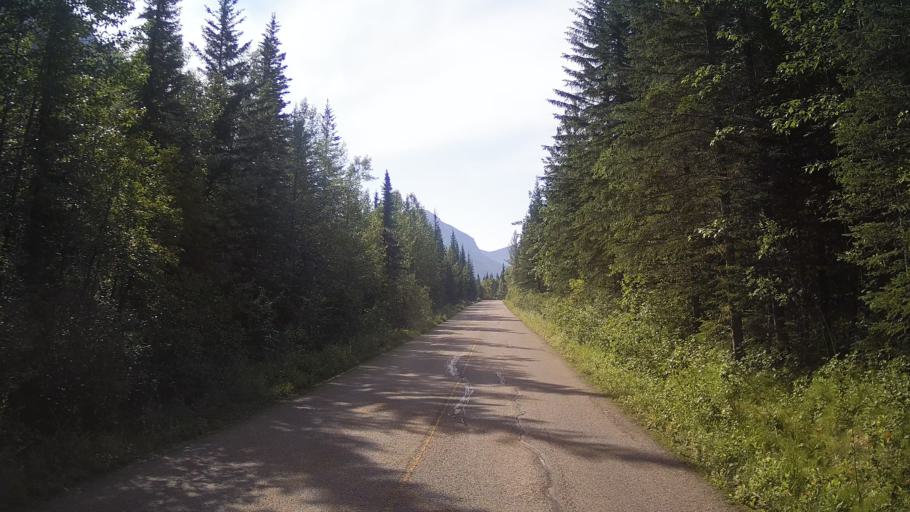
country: CA
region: Alberta
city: Hinton
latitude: 53.1760
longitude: -117.8310
